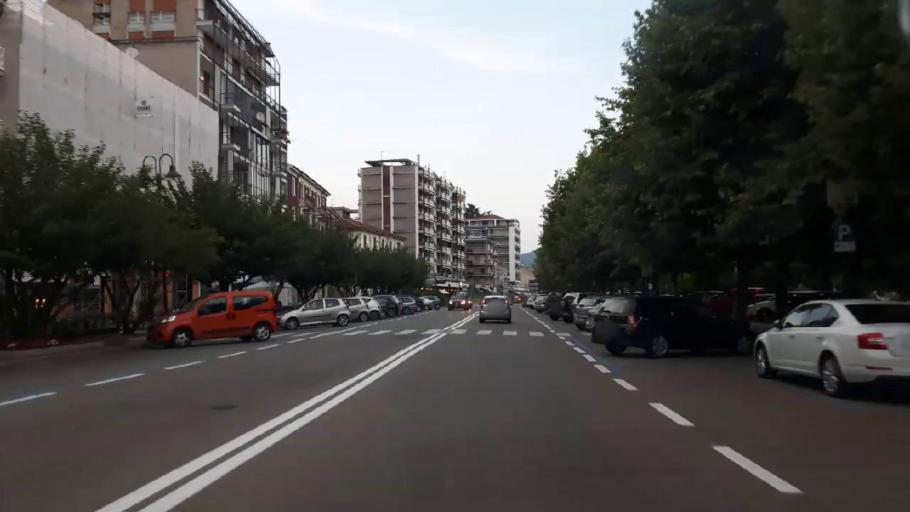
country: IT
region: Piedmont
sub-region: Provincia di Novara
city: Arona
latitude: 45.7569
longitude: 8.5600
